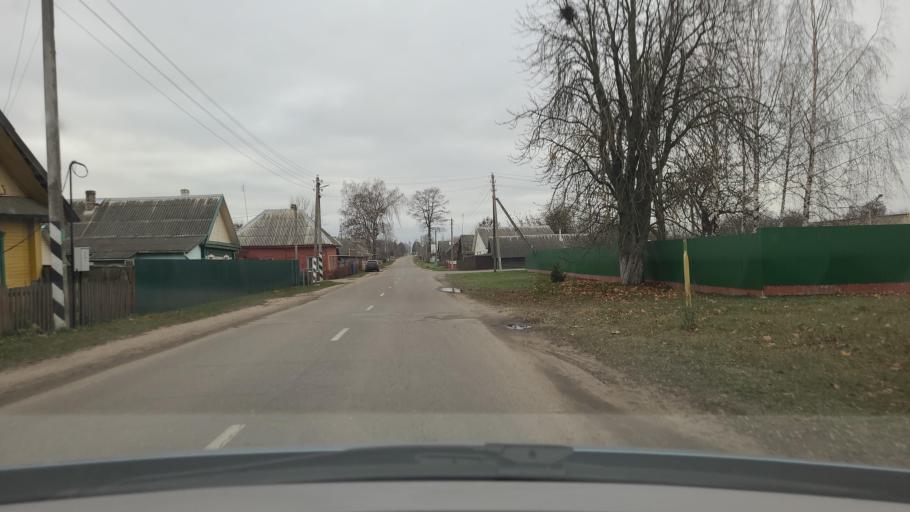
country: BY
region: Minsk
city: Khalopyenichy
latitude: 54.5174
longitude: 28.9576
